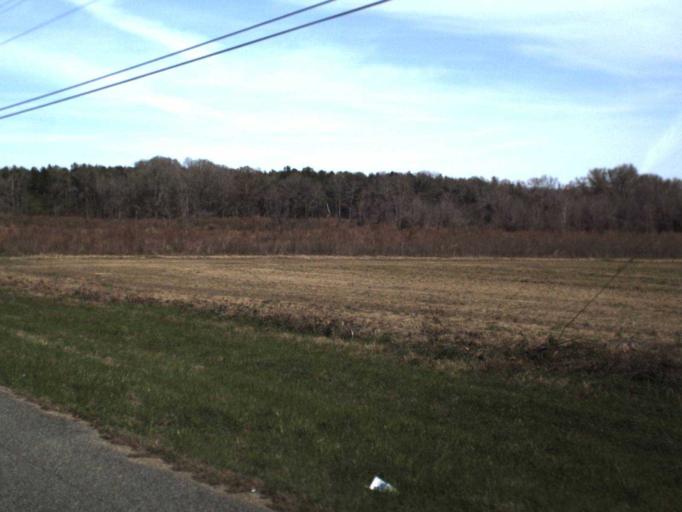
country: US
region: Florida
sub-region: Jackson County
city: Graceville
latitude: 30.9107
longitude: -85.5215
